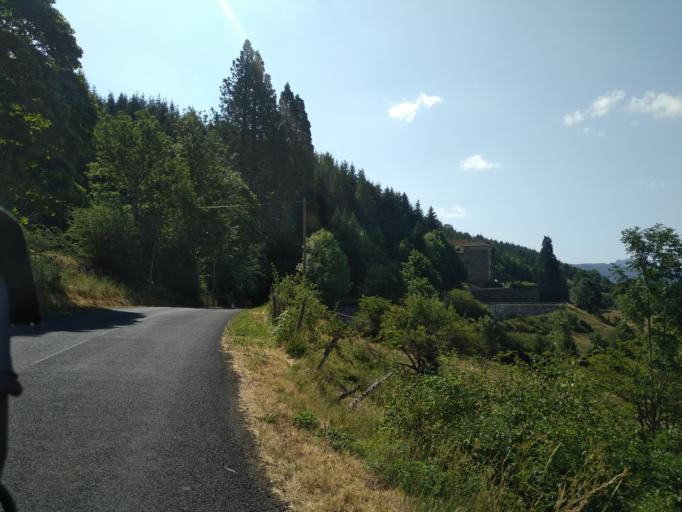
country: FR
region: Auvergne
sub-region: Departement du Cantal
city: Riom-es-Montagnes
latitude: 45.1999
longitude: 2.7170
